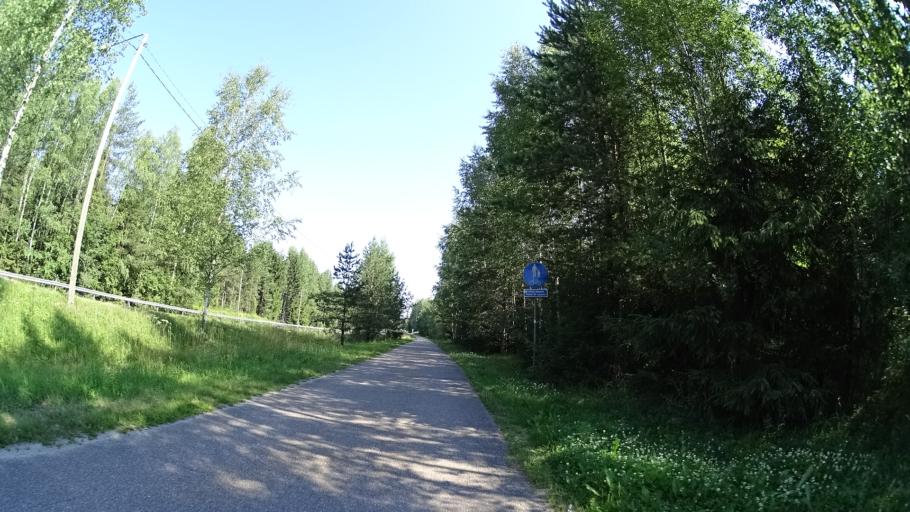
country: FI
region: Uusimaa
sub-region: Helsinki
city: Kerava
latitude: 60.3329
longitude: 25.1248
